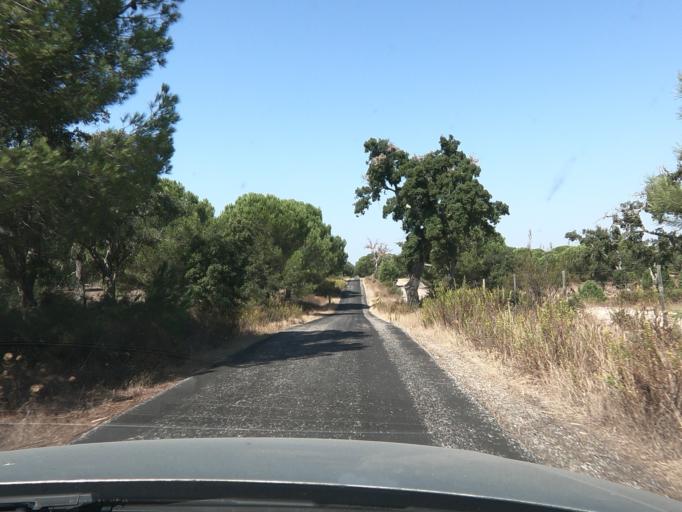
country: PT
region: Setubal
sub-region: Alcacer do Sal
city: Alcacer do Sal
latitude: 38.2617
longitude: -8.3099
